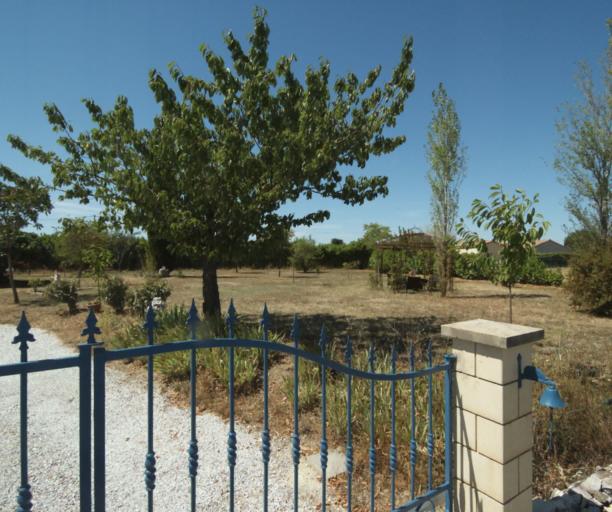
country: FR
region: Midi-Pyrenees
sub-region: Departement de la Haute-Garonne
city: Saint-Felix-Lauragais
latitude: 43.4811
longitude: 1.9175
